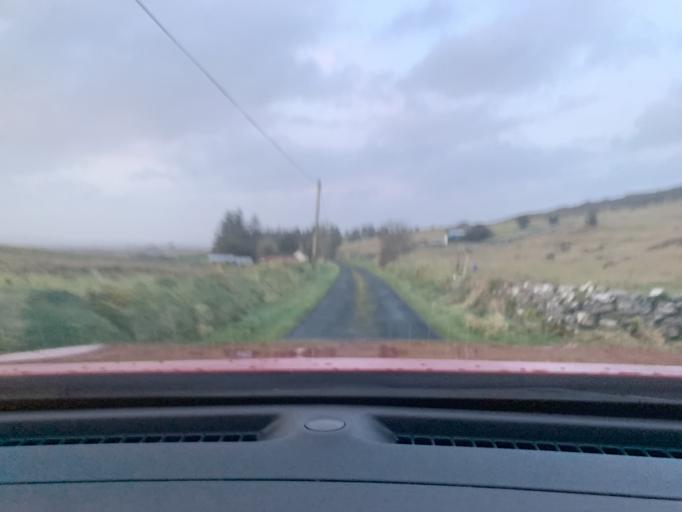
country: IE
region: Connaught
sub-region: Sligo
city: Ballymote
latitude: 54.0528
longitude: -8.3966
